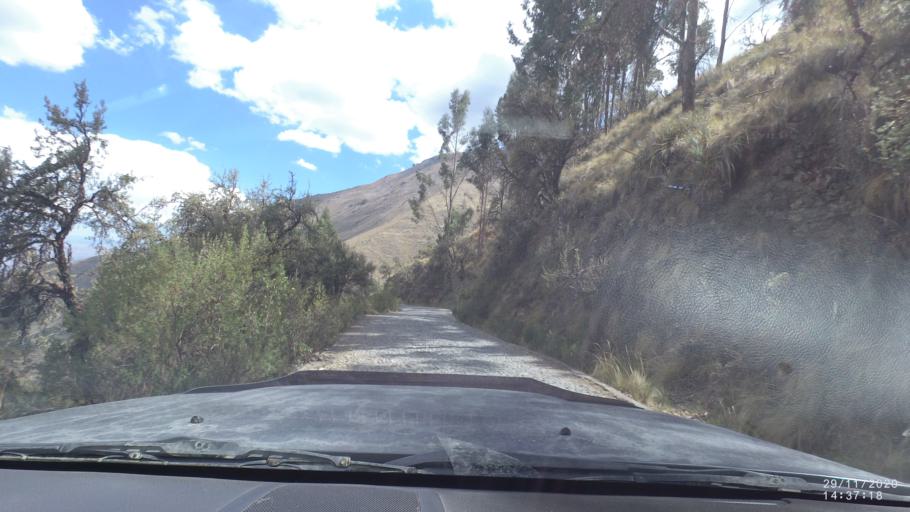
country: BO
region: Cochabamba
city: Sipe Sipe
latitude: -17.2702
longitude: -66.3289
